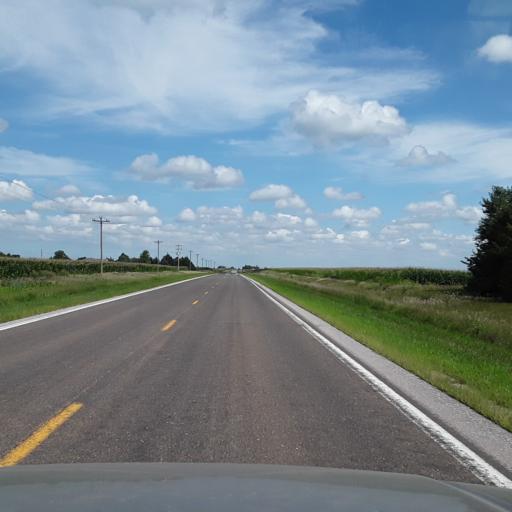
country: US
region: Nebraska
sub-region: Polk County
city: Osceola
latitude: 41.0475
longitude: -97.4064
